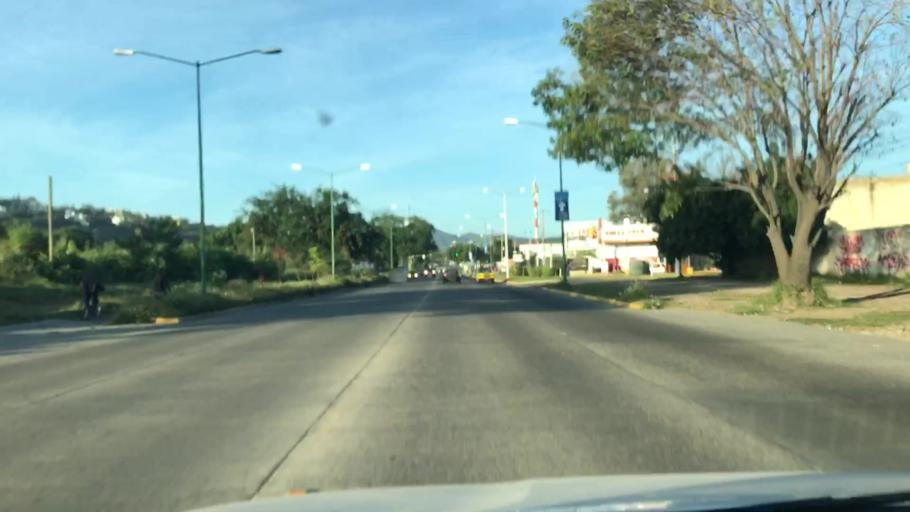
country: MX
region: Jalisco
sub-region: Tlajomulco de Zuniga
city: Palomar
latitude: 20.6279
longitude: -103.4588
